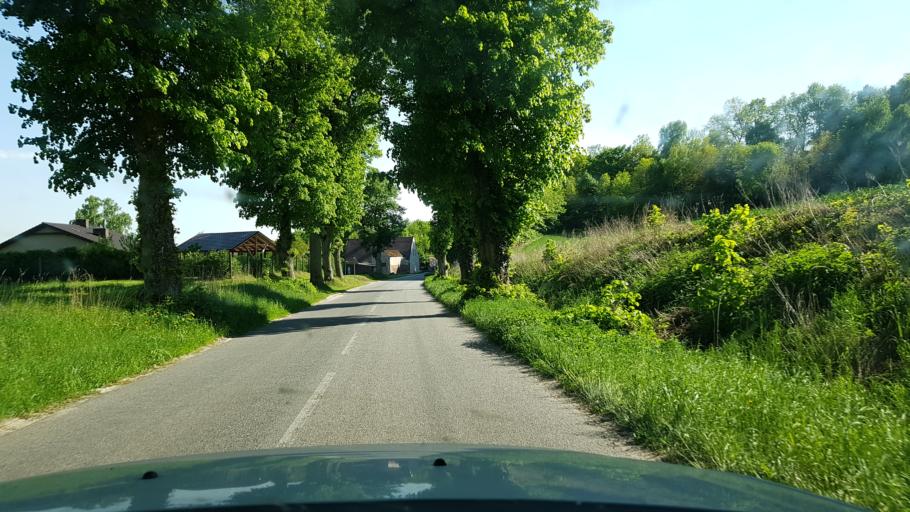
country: PL
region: West Pomeranian Voivodeship
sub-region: Powiat lobeski
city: Resko
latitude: 53.7793
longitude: 15.4094
